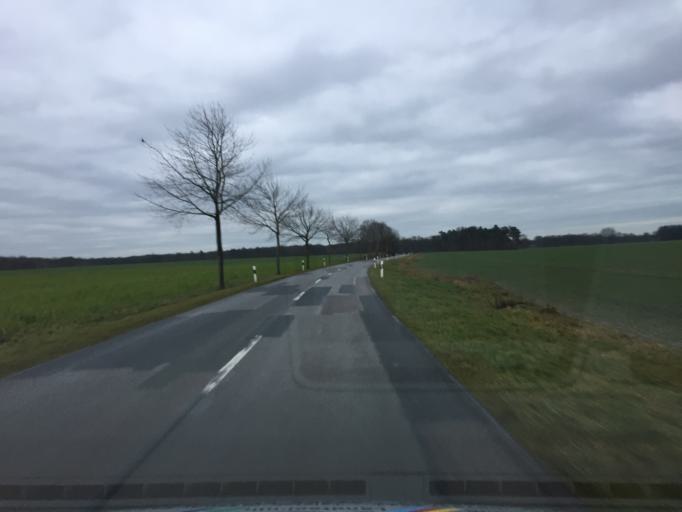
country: DE
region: Lower Saxony
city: Borstel
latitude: 52.6558
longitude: 8.9865
